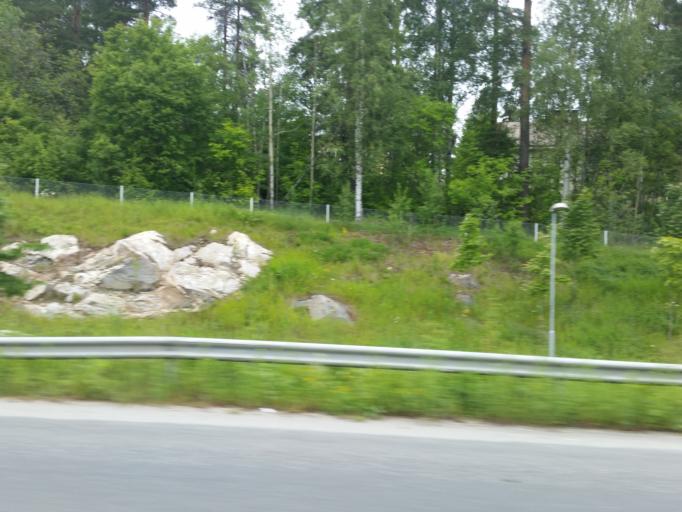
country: FI
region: Northern Savo
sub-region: Kuopio
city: Kuopio
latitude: 62.8817
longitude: 27.6549
